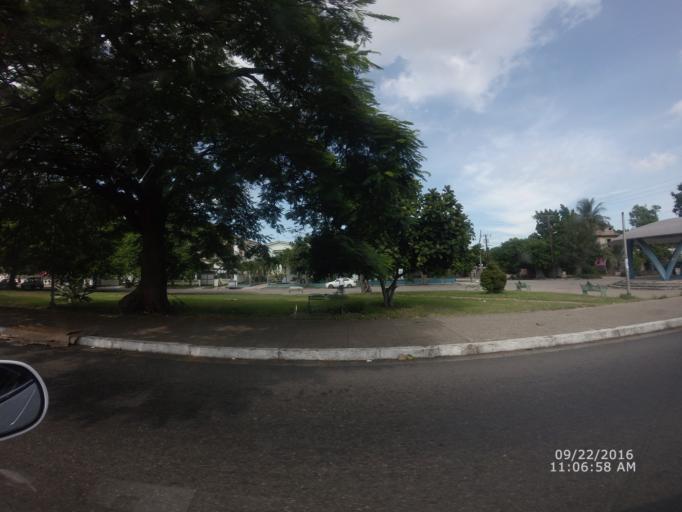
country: CU
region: La Habana
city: Havana
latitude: 23.1166
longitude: -82.4174
